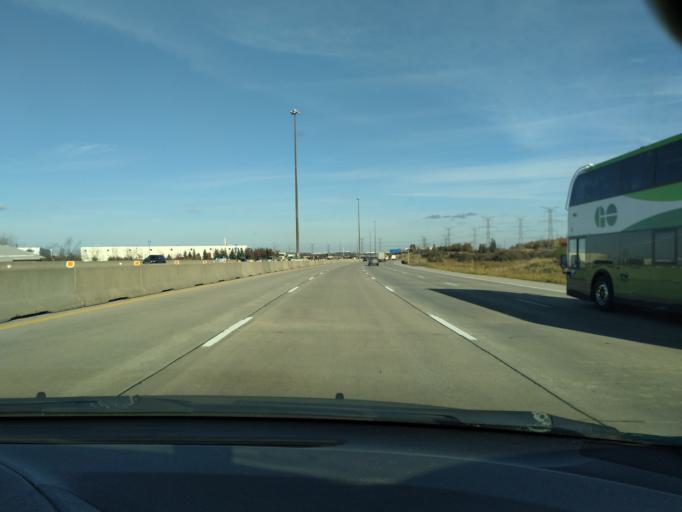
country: CA
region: Ontario
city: Brampton
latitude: 43.6129
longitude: -79.7777
